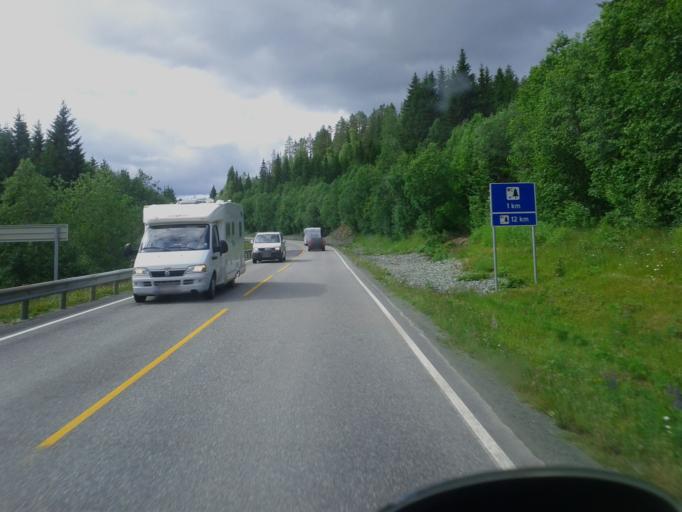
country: NO
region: Nord-Trondelag
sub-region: Grong
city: Grong
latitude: 64.5402
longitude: 12.4477
